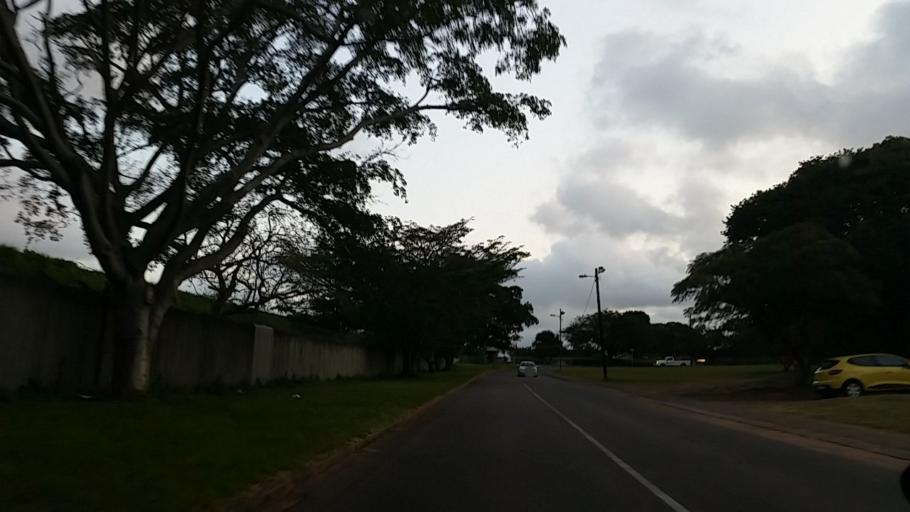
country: ZA
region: KwaZulu-Natal
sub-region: eThekwini Metropolitan Municipality
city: Berea
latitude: -29.8545
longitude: 30.9107
